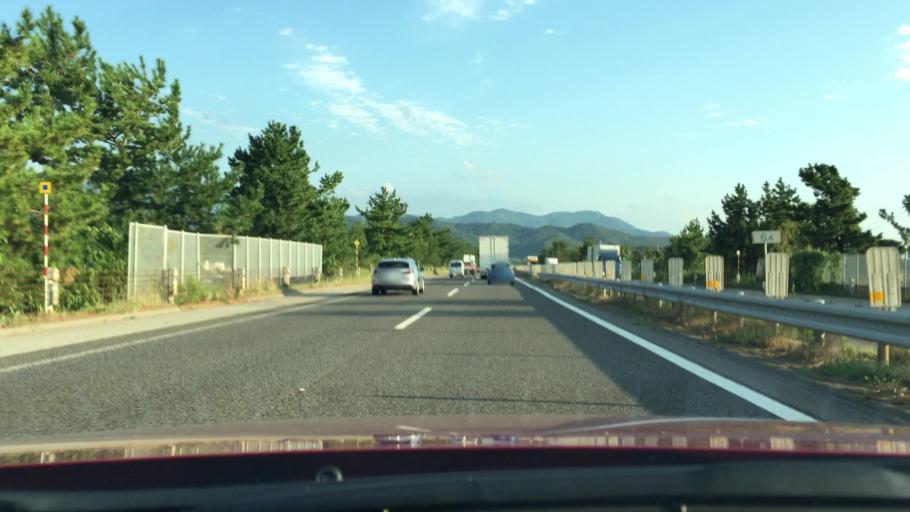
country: JP
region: Shiga Prefecture
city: Nagahama
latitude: 35.3720
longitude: 136.3040
